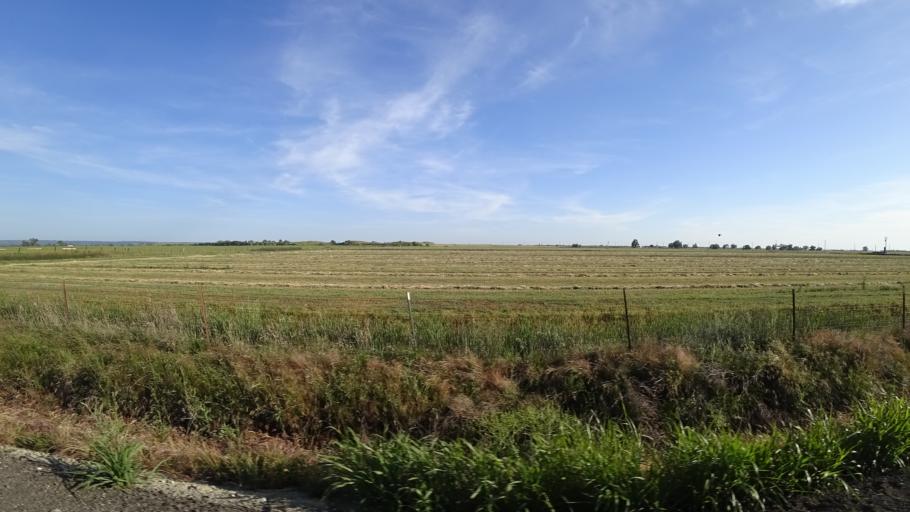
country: US
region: California
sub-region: Placer County
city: Lincoln
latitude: 38.9264
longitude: -121.3163
